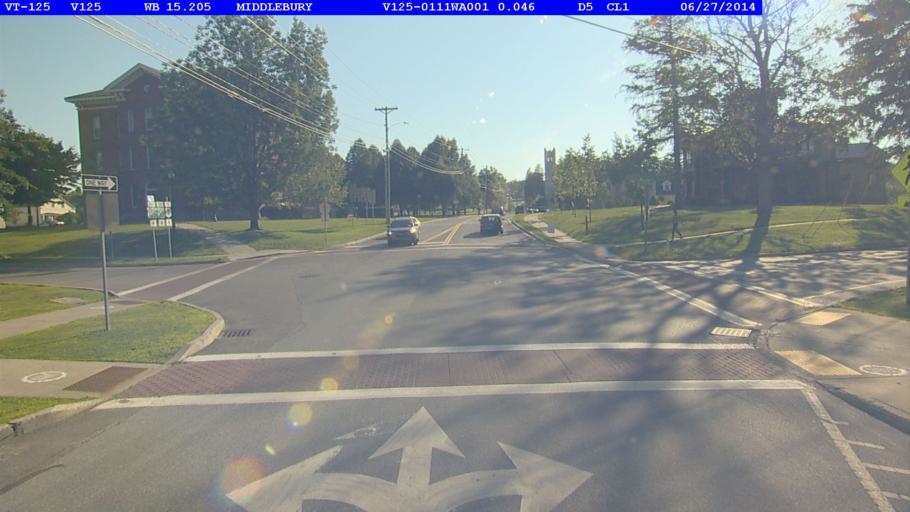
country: US
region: Vermont
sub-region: Addison County
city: Middlebury (village)
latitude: 44.0114
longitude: -73.1714
